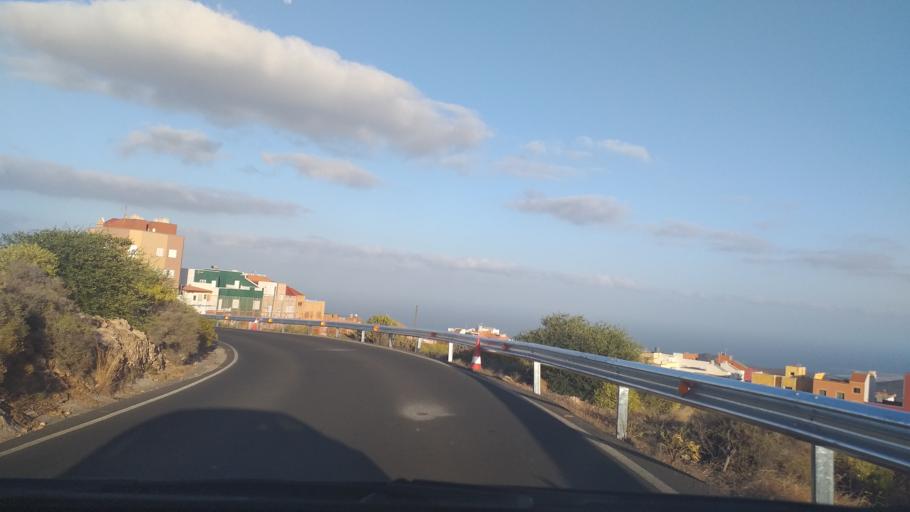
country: ES
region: Canary Islands
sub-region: Provincia de Las Palmas
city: Ingenio
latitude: 27.9213
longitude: -15.4513
